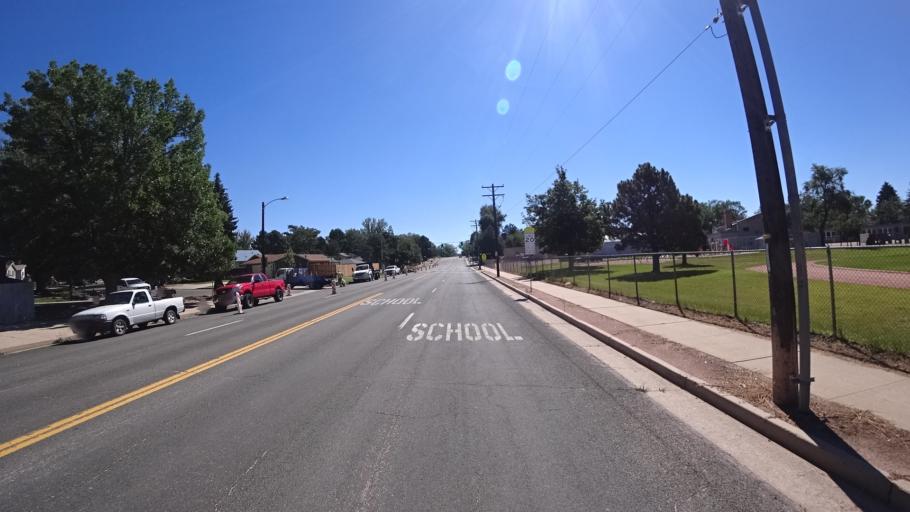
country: US
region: Colorado
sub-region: El Paso County
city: Colorado Springs
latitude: 38.8677
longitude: -104.8031
